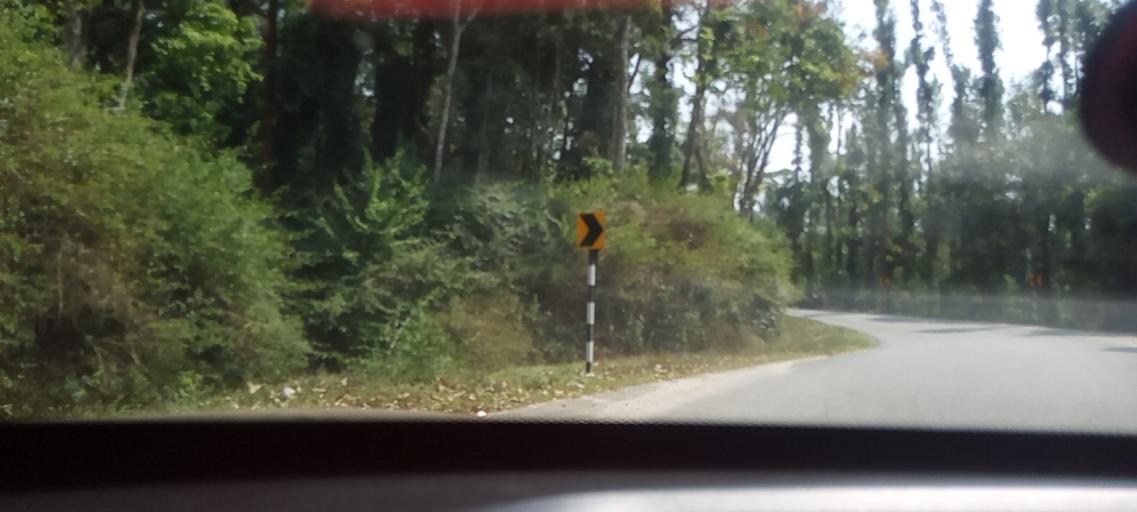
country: IN
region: Karnataka
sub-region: Chikmagalur
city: Mudigere
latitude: 13.2631
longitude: 75.6293
